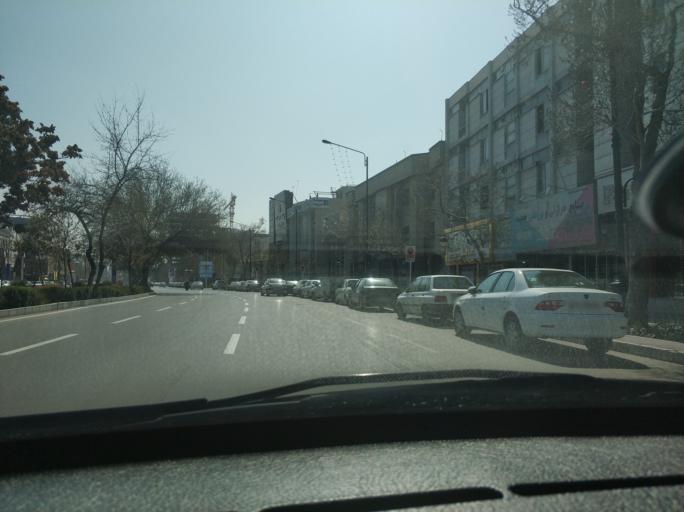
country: IR
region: Razavi Khorasan
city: Mashhad
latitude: 36.2951
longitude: 59.5766
